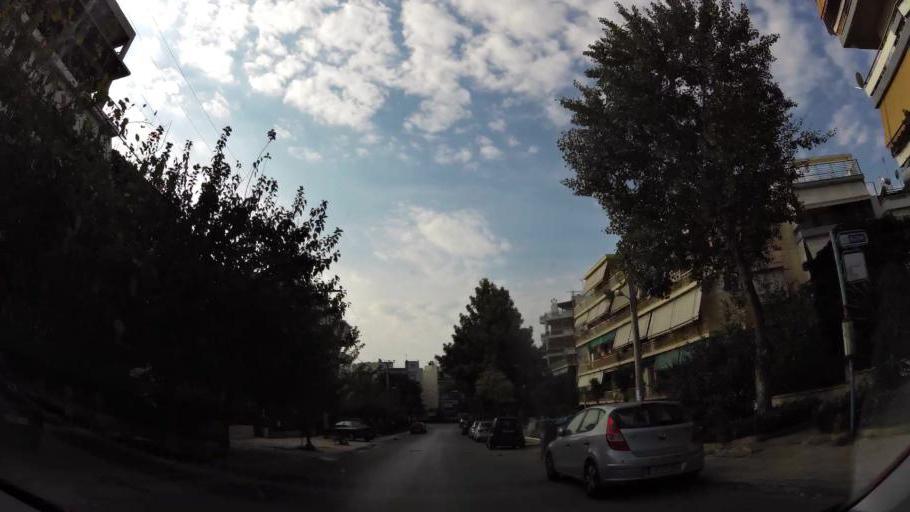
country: GR
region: Attica
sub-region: Nomarchia Athinas
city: Nea Smyrni
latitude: 37.9404
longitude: 23.7054
